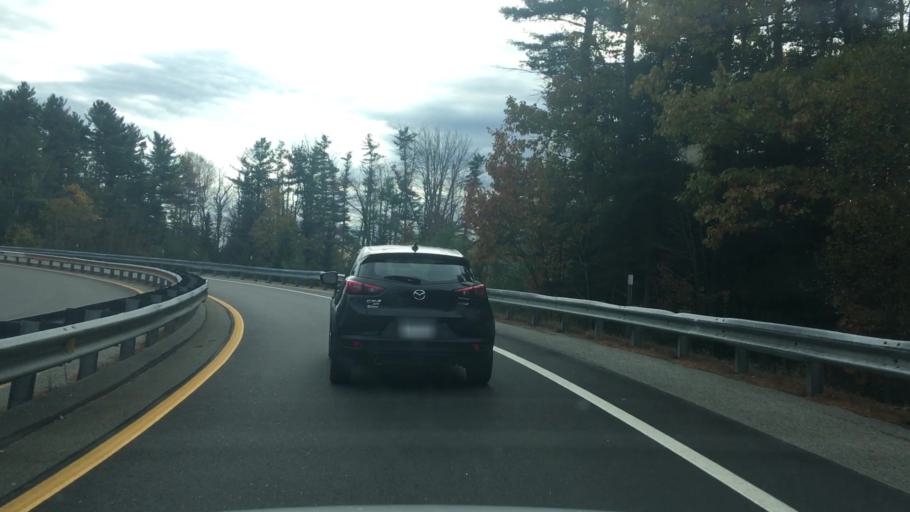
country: US
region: Maine
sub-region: York County
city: Biddeford
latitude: 43.4812
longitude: -70.5017
